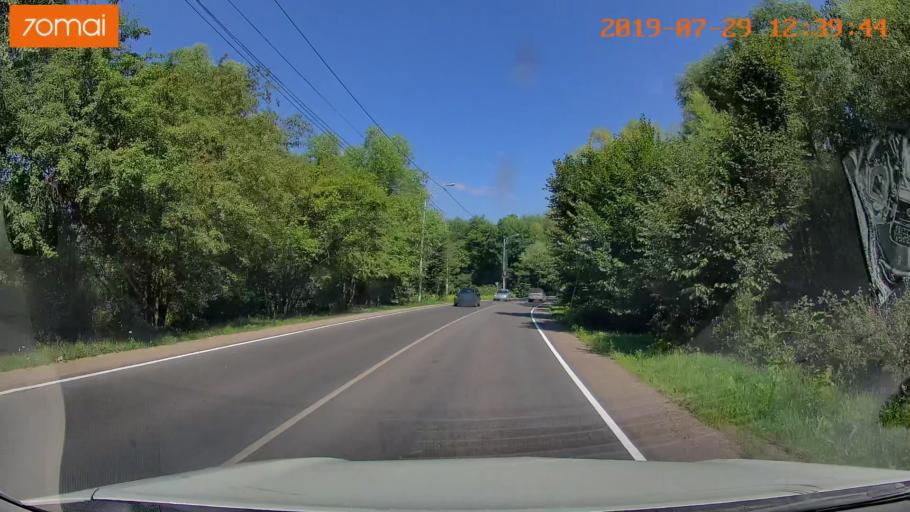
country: RU
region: Kaliningrad
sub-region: Gorod Kaliningrad
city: Kaliningrad
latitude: 54.6633
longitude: 20.5406
